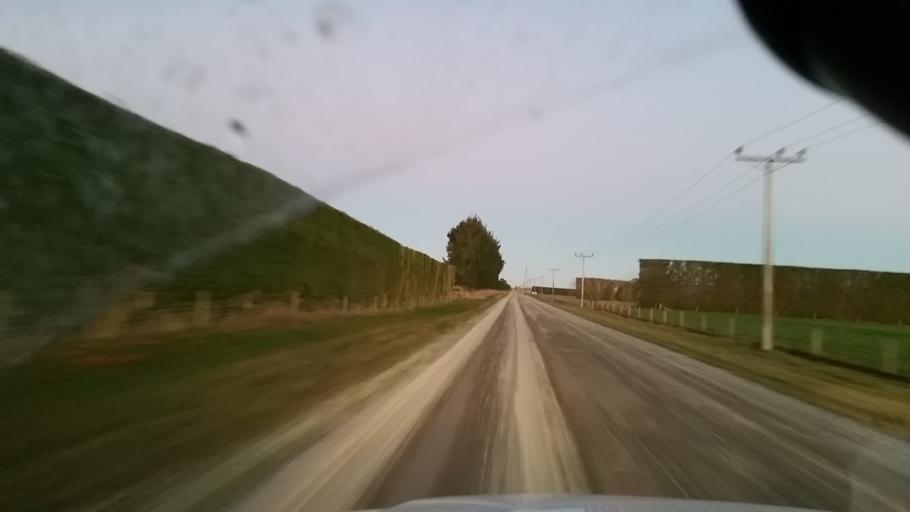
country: NZ
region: Canterbury
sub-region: Ashburton District
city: Tinwald
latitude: -43.9745
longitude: 171.6409
